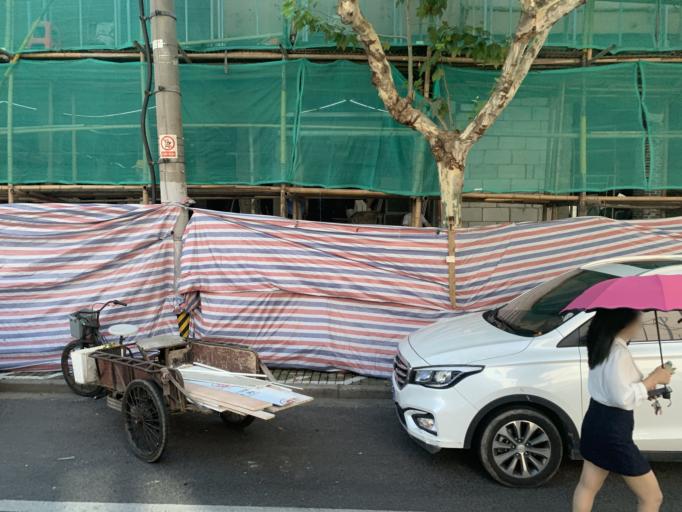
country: CN
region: Shanghai Shi
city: Pudong
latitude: 31.2271
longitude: 121.5096
